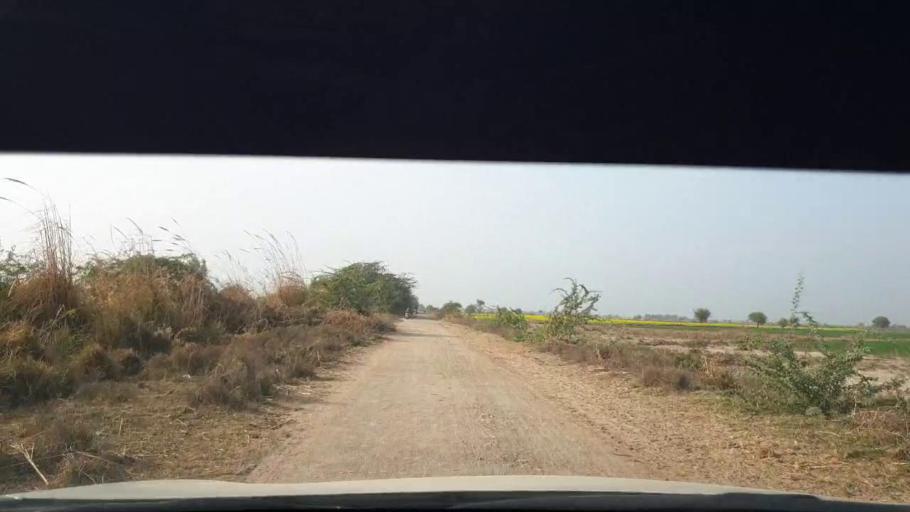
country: PK
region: Sindh
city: Berani
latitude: 25.7485
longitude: 68.9446
